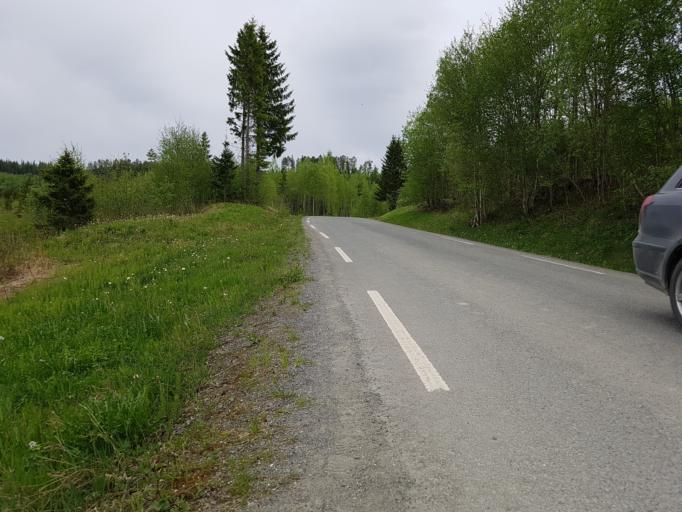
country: NO
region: Nord-Trondelag
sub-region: Levanger
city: Skogn
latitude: 63.6311
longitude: 11.2759
